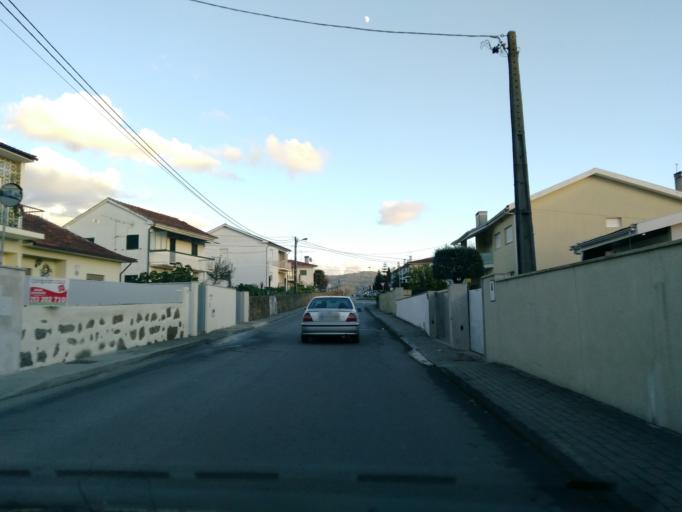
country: PT
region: Braga
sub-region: Braga
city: Braga
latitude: 41.5287
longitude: -8.4558
